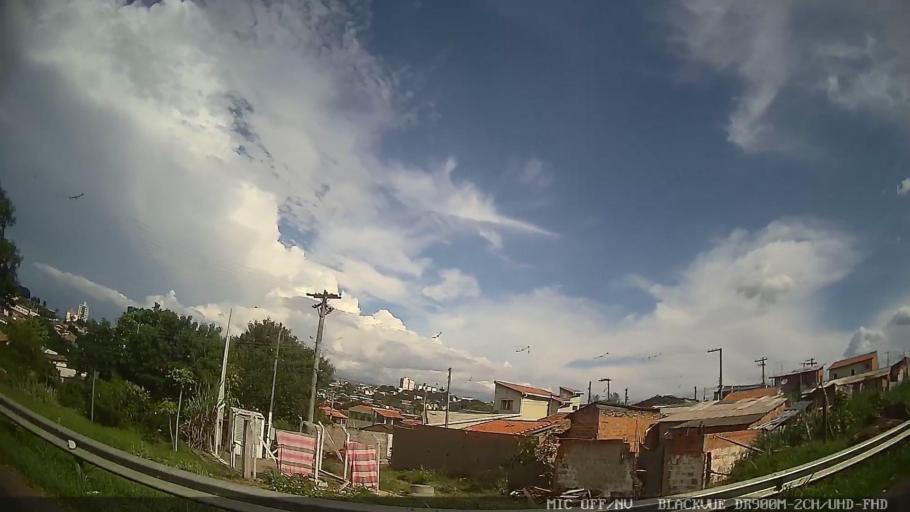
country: BR
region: Sao Paulo
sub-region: Laranjal Paulista
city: Laranjal Paulista
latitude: -23.0432
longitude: -47.8428
